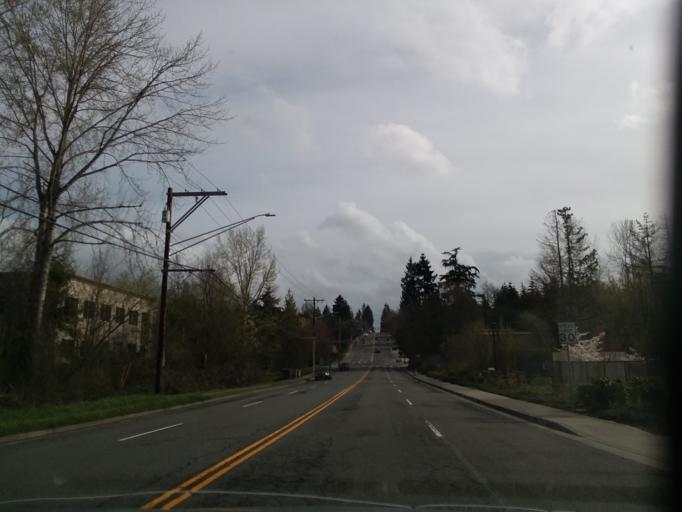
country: US
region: Washington
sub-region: Snohomish County
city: Lynnwood
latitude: 47.8045
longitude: -122.3220
